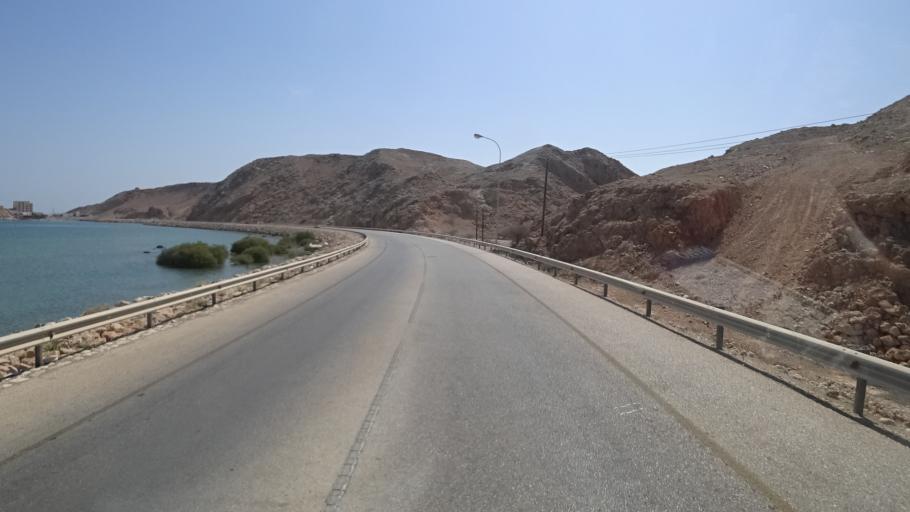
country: OM
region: Ash Sharqiyah
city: Sur
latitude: 22.5531
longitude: 59.5355
